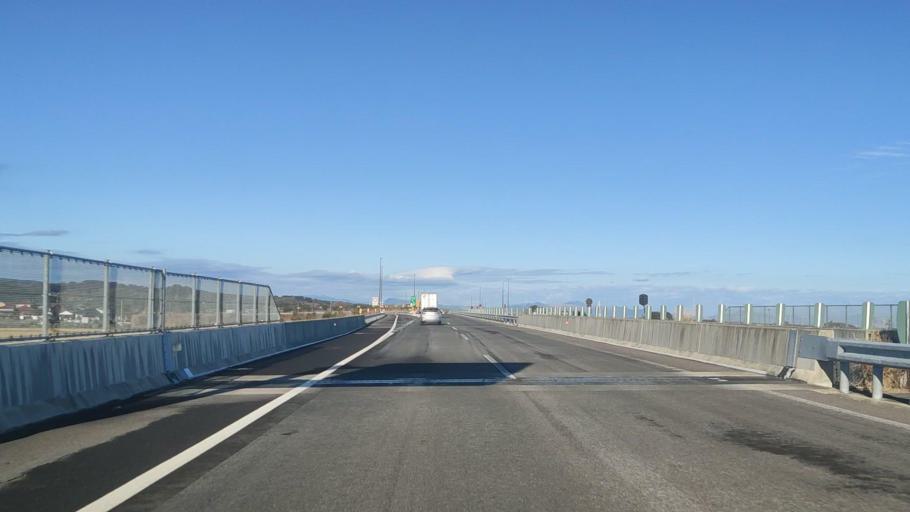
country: JP
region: Fukuoka
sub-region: Buzen-shi
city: Buzen
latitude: 33.5850
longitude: 131.1298
